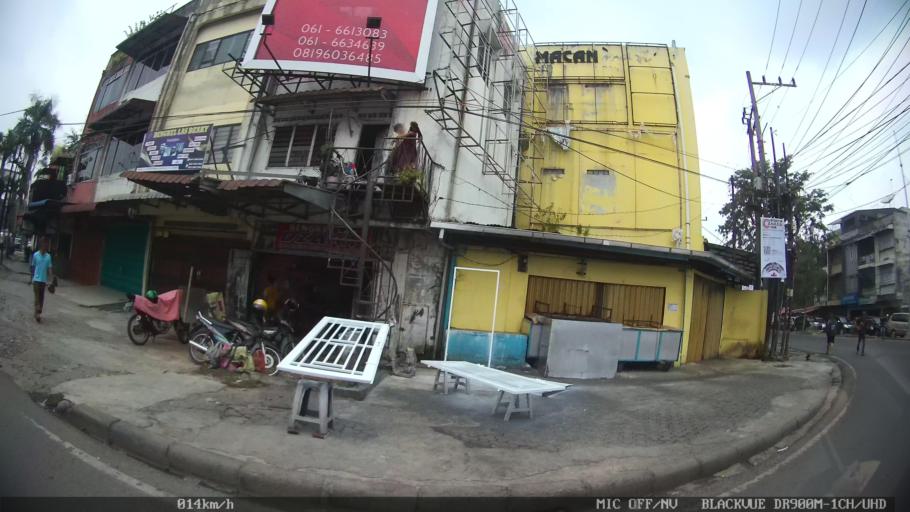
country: ID
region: North Sumatra
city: Medan
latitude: 3.5724
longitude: 98.6860
